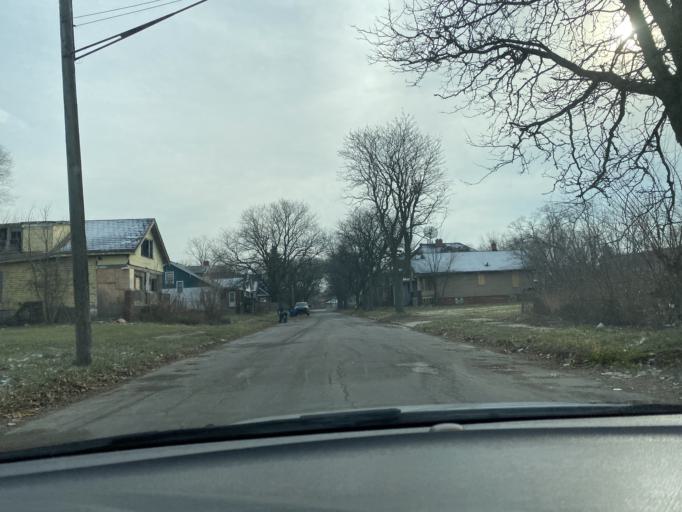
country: US
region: Michigan
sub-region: Wayne County
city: Highland Park
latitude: 42.3683
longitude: -83.1292
